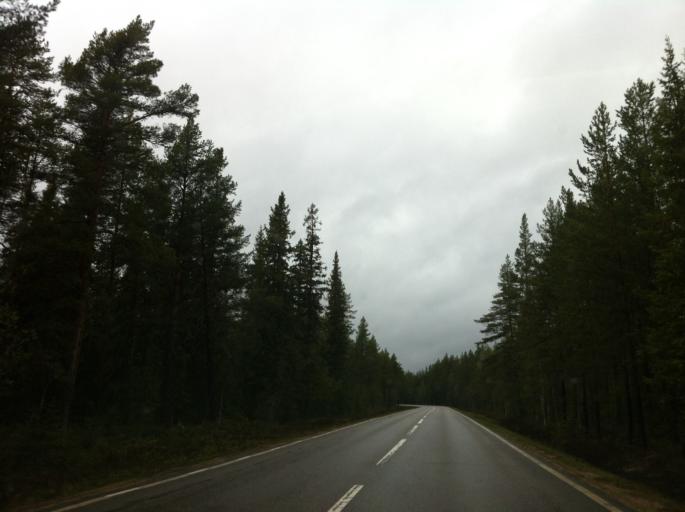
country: SE
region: Jaemtland
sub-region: Harjedalens Kommun
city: Sveg
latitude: 62.1437
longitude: 13.9737
